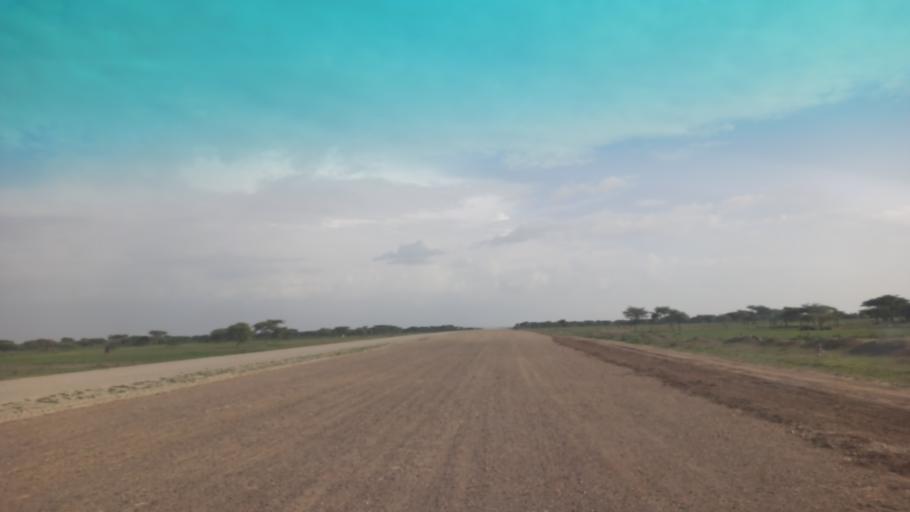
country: ET
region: Oromiya
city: Ziway
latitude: 7.6531
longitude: 38.6829
